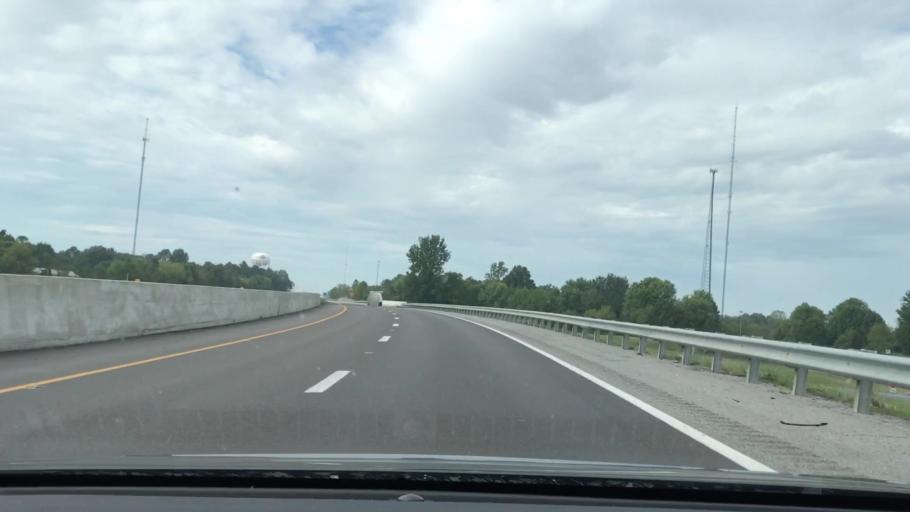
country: US
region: Kentucky
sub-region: Graves County
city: Mayfield
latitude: 36.7683
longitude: -88.6417
